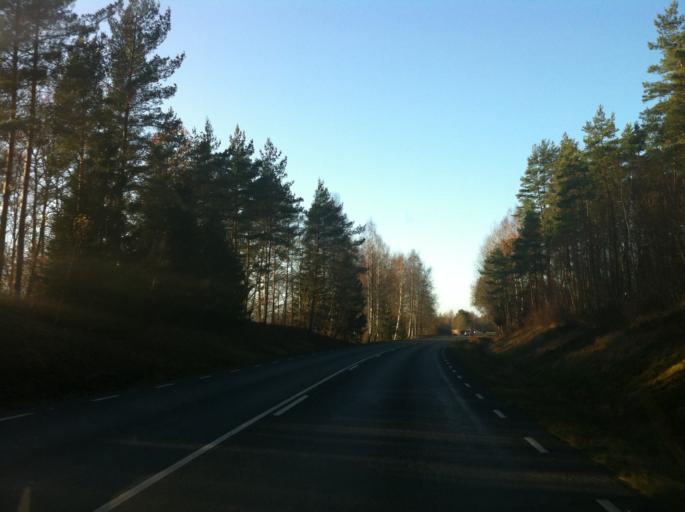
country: SE
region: Skane
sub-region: Kristianstads Kommun
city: Tollarp
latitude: 56.1754
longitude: 14.2978
